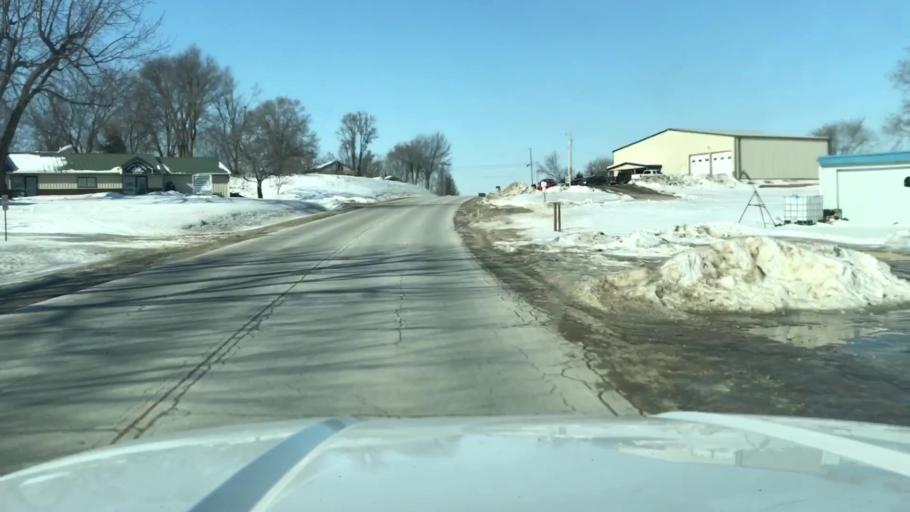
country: US
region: Missouri
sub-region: Andrew County
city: Savannah
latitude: 39.9475
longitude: -94.8397
